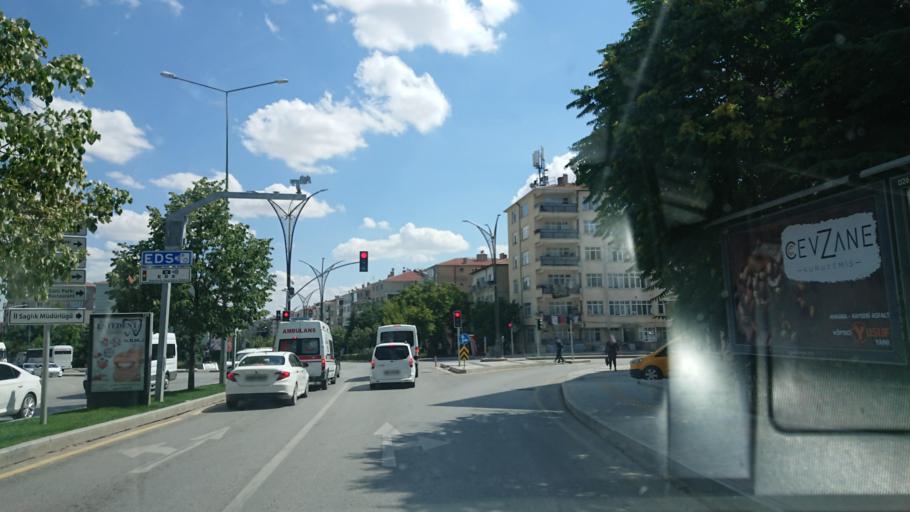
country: TR
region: Kirsehir
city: Kirsehir
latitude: 39.1551
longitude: 34.1594
